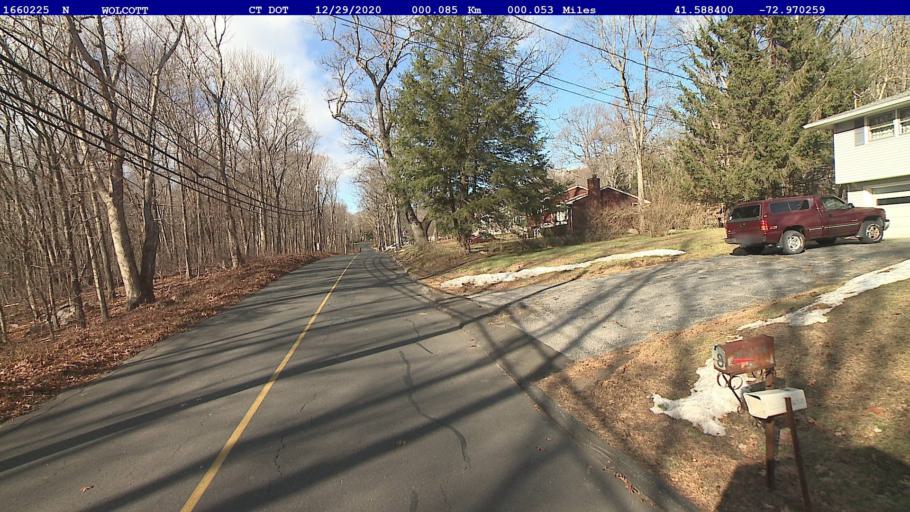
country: US
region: Connecticut
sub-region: New Haven County
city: Wolcott
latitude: 41.5884
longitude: -72.9703
